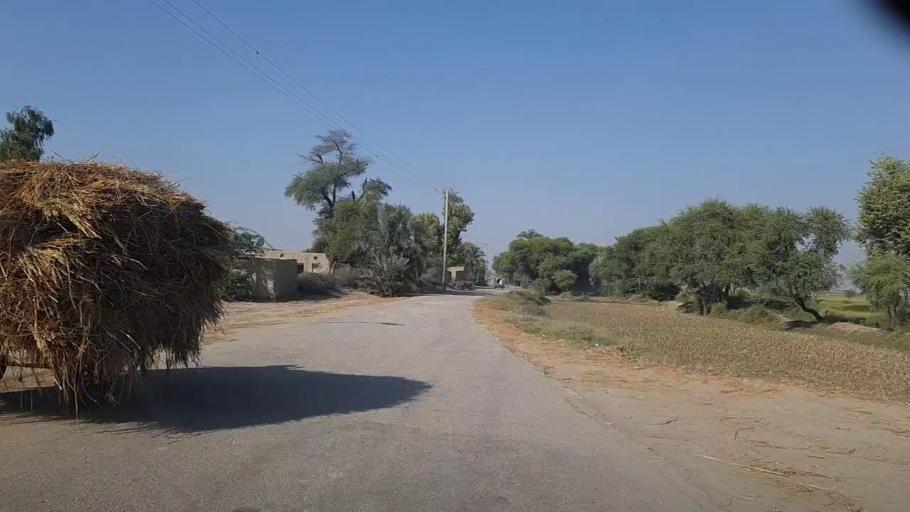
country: PK
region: Sindh
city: Tangwani
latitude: 28.2454
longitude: 68.9964
